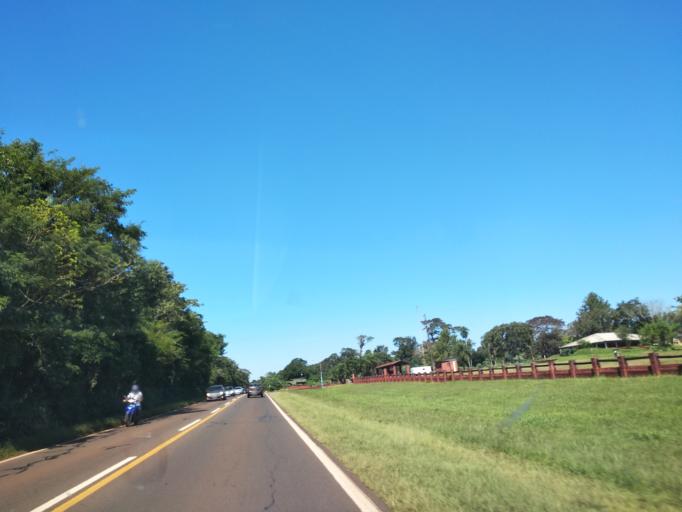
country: AR
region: Misiones
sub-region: Departamento de Iguazu
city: Puerto Iguazu
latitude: -25.6366
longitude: -54.5381
